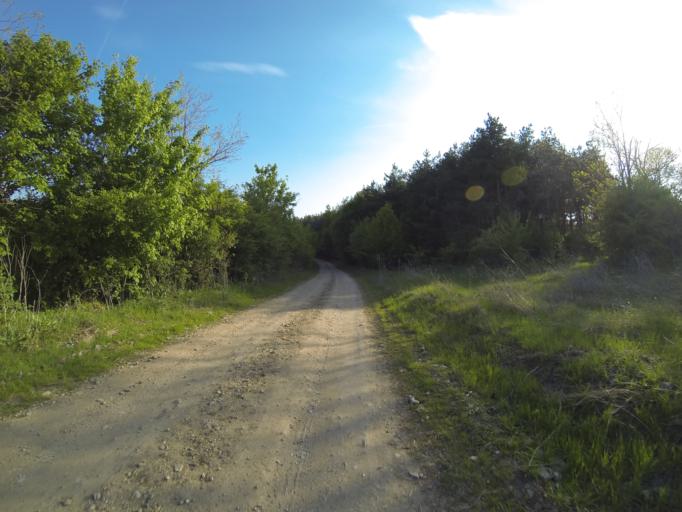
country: RO
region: Dolj
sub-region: Comuna Filiasi
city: Fratostita
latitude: 44.5624
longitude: 23.5860
